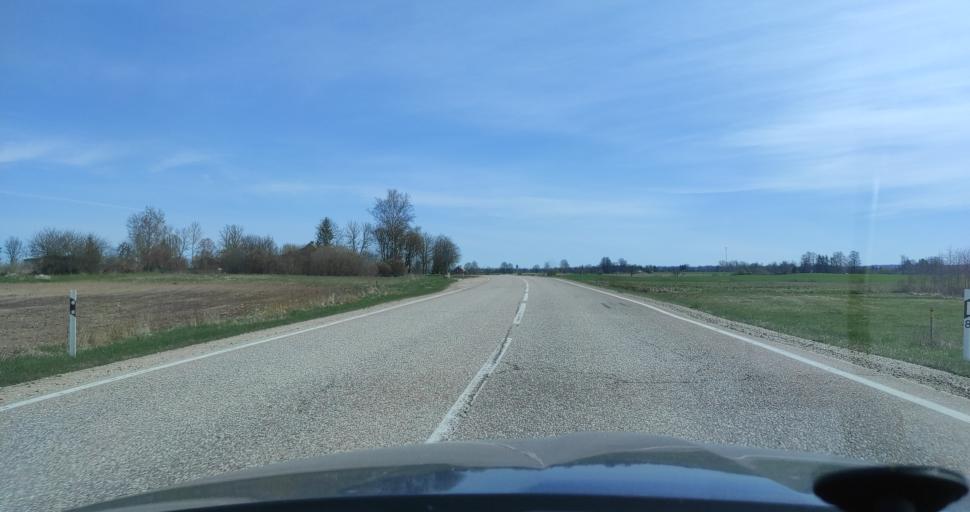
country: LV
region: Talsu Rajons
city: Stende
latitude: 57.2094
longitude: 22.4700
